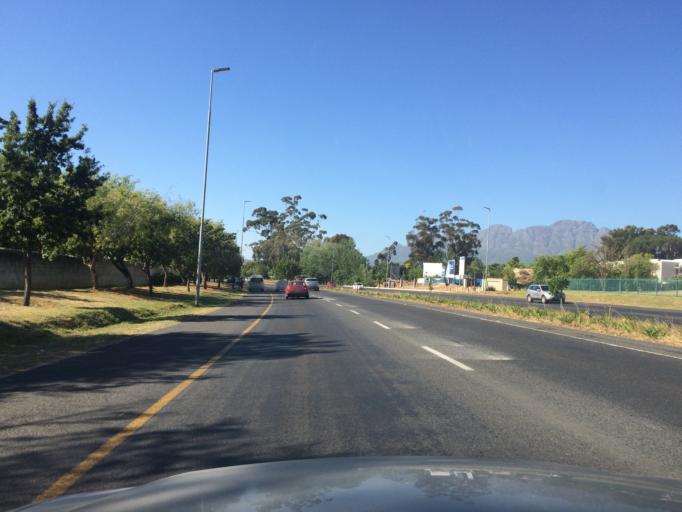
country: ZA
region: Western Cape
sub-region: Cape Winelands District Municipality
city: Stellenbosch
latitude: -33.9556
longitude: 18.8554
